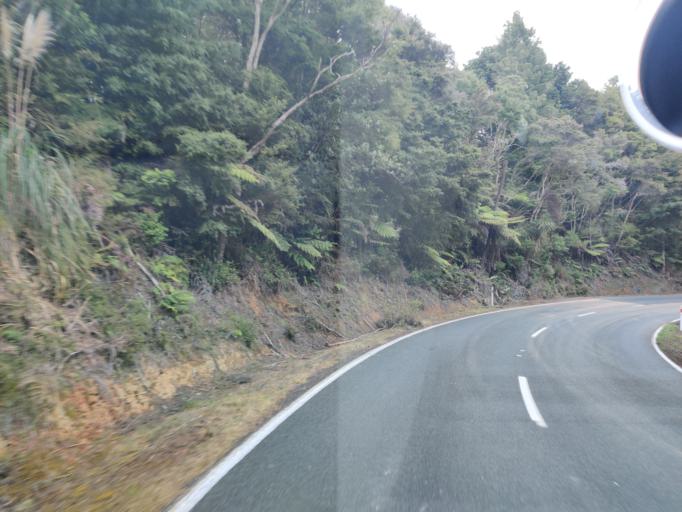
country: NZ
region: Northland
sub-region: Whangarei
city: Ngunguru
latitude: -35.5782
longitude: 174.4064
